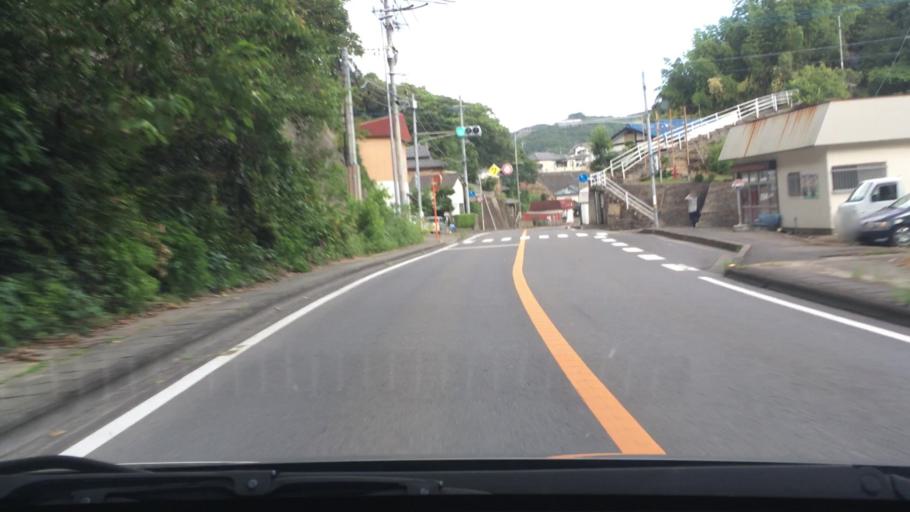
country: JP
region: Nagasaki
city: Togitsu
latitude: 32.8271
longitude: 129.7714
